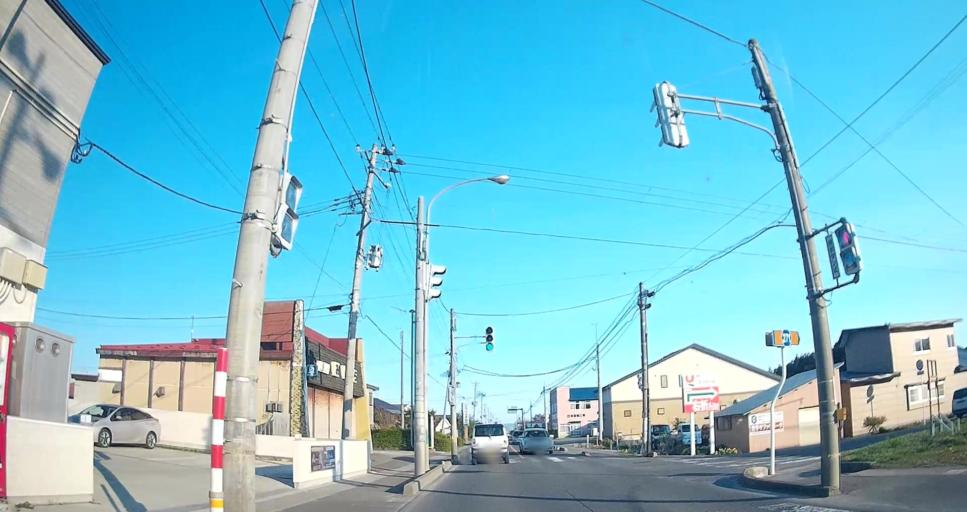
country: JP
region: Aomori
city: Mutsu
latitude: 41.2727
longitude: 141.2166
